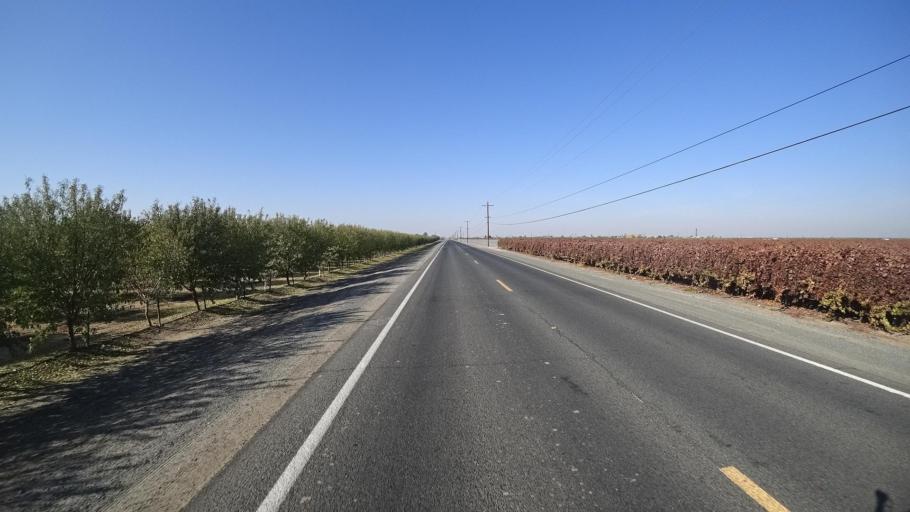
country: US
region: California
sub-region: Kern County
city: Delano
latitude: 35.7614
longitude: -119.2089
